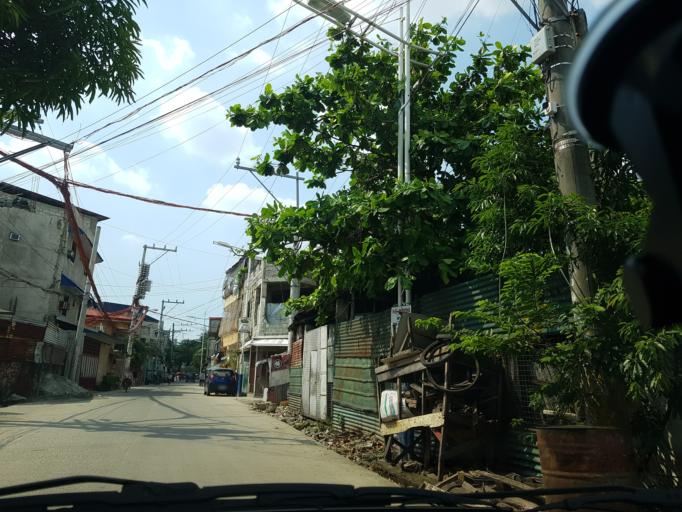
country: PH
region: Calabarzon
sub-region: Province of Rizal
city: Pateros
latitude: 14.5452
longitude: 121.0843
